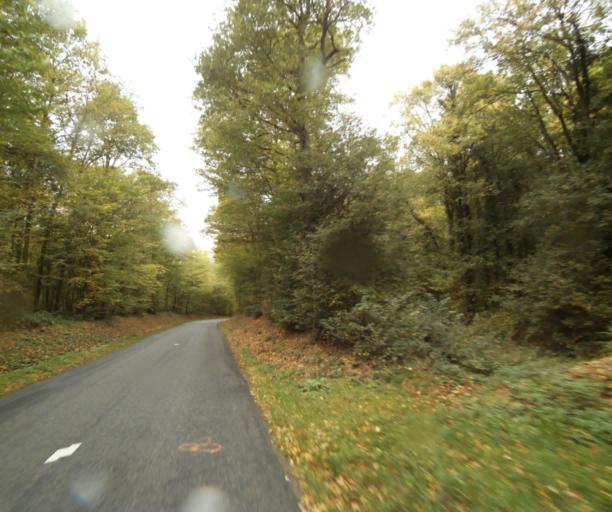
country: FR
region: Centre
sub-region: Departement d'Eure-et-Loir
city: Vert-en-Drouais
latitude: 48.7574
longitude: 1.3319
